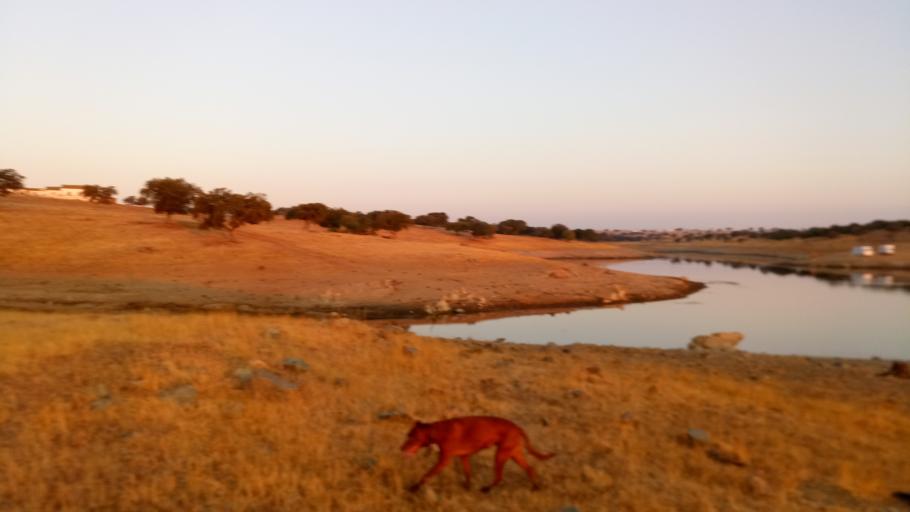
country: PT
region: Evora
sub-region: Mourao
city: Mourao
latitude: 38.3528
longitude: -7.4418
